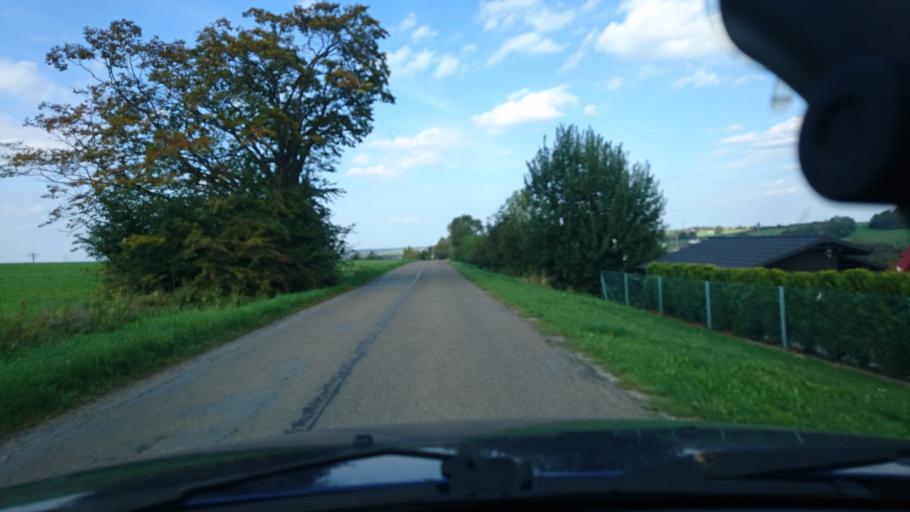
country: PL
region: Silesian Voivodeship
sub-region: Powiat bielski
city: Jasienica
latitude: 49.8290
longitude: 18.9323
